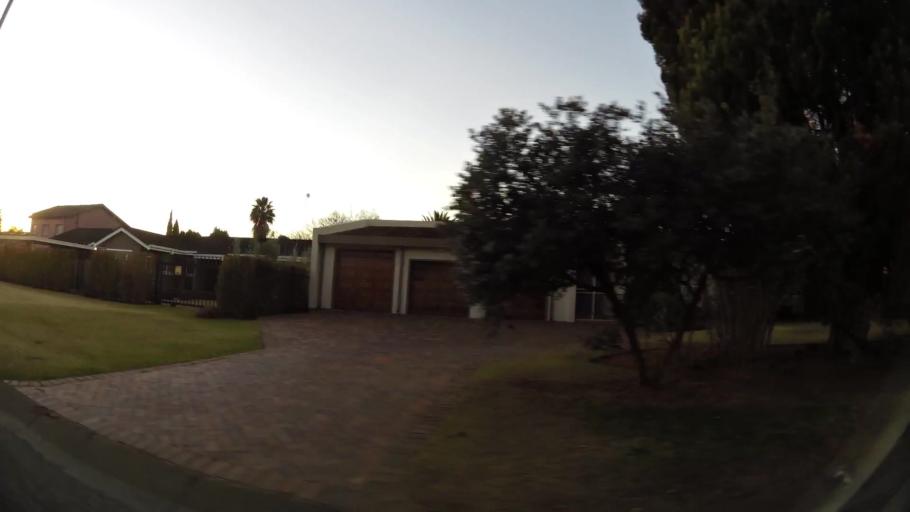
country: ZA
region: North-West
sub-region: Dr Kenneth Kaunda District Municipality
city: Potchefstroom
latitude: -26.7227
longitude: 27.1144
